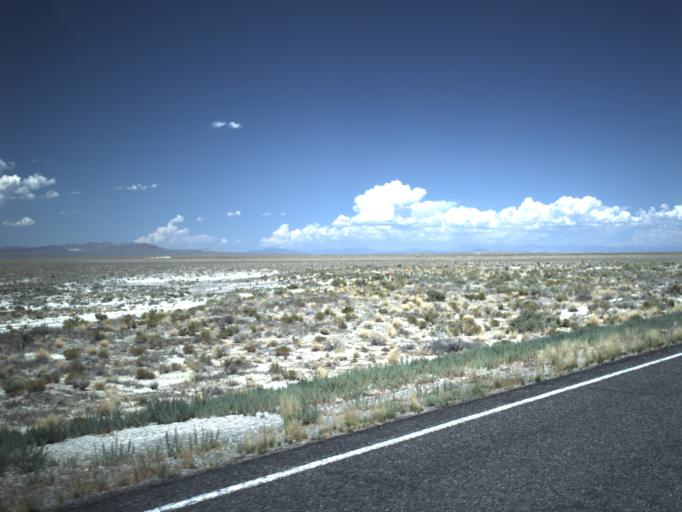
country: US
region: Utah
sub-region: Millard County
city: Delta
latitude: 39.1912
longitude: -112.9990
